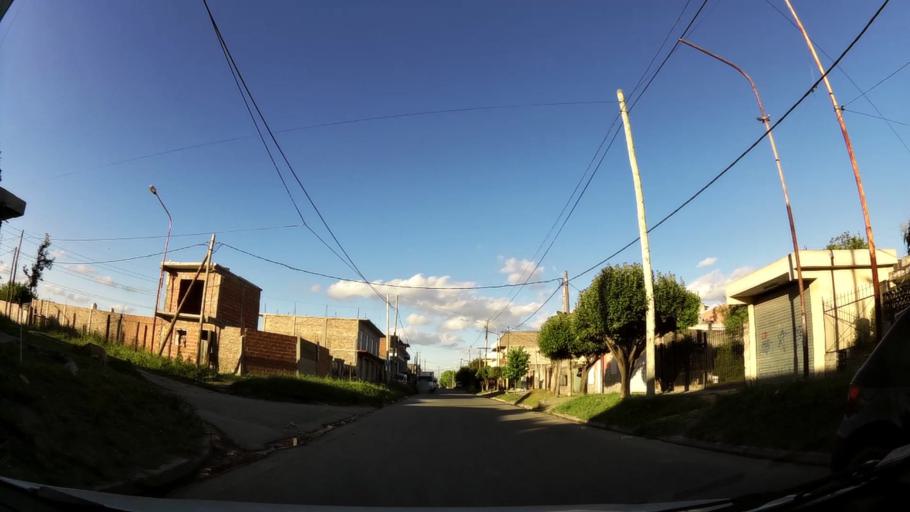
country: AR
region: Buenos Aires
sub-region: Partido de Moron
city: Moron
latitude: -34.7129
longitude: -58.6179
